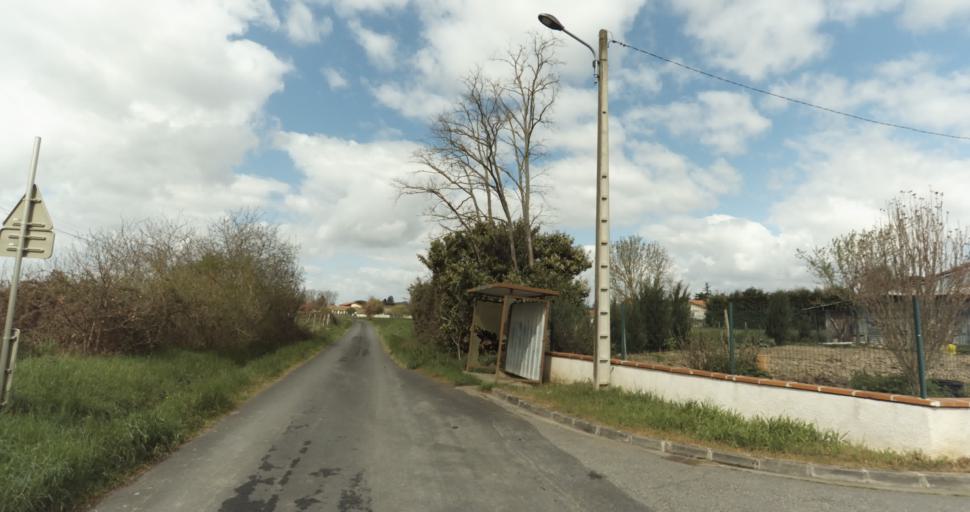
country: FR
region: Midi-Pyrenees
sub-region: Departement de la Haute-Garonne
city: Auterive
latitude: 43.3335
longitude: 1.4832
